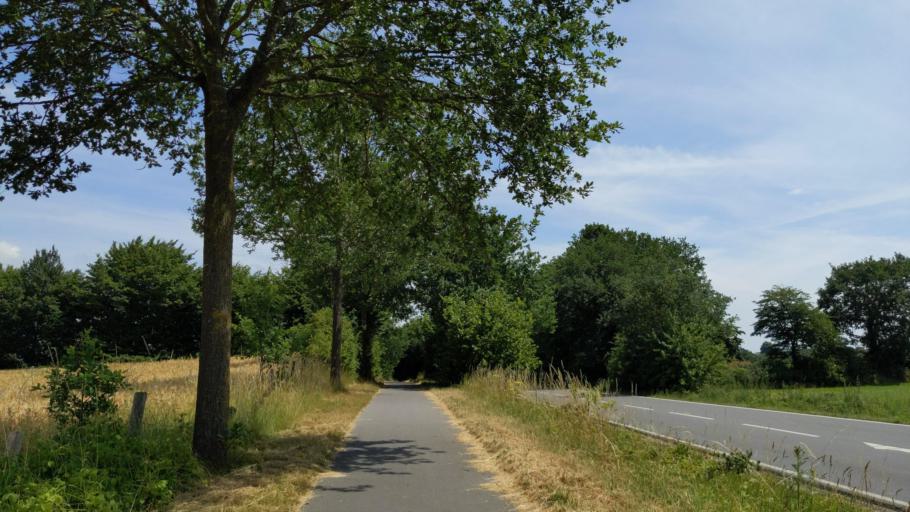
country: DE
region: Schleswig-Holstein
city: Bosdorf
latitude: 54.1486
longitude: 10.5094
